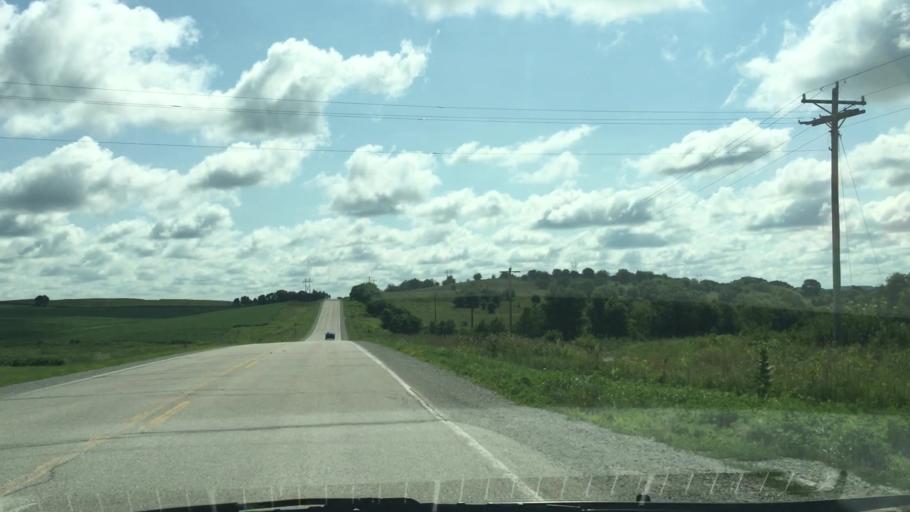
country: US
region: Iowa
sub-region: Johnson County
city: Solon
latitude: 41.8312
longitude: -91.4927
